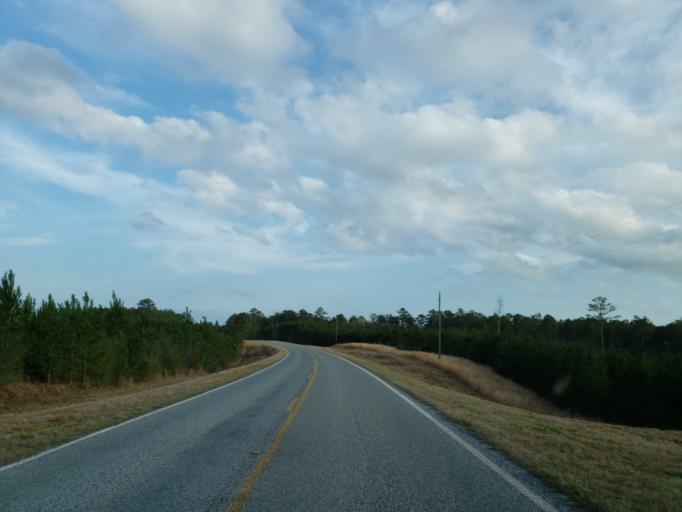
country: US
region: Mississippi
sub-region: Clarke County
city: Stonewall
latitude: 32.1765
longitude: -88.7036
